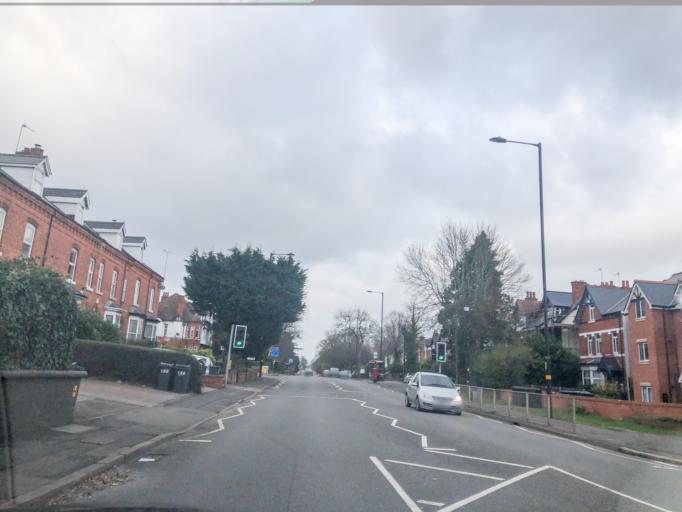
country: GB
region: England
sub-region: City and Borough of Birmingham
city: Birmingham
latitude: 52.4250
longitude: -1.8924
